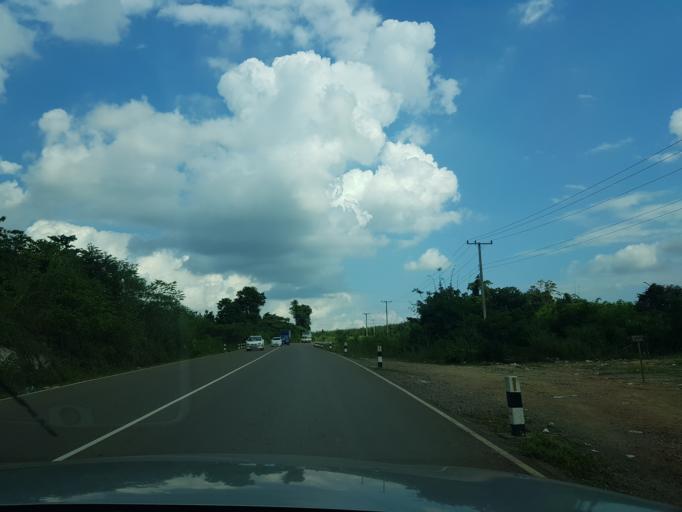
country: TH
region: Nong Khai
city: Sangkhom
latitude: 18.0378
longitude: 102.3620
